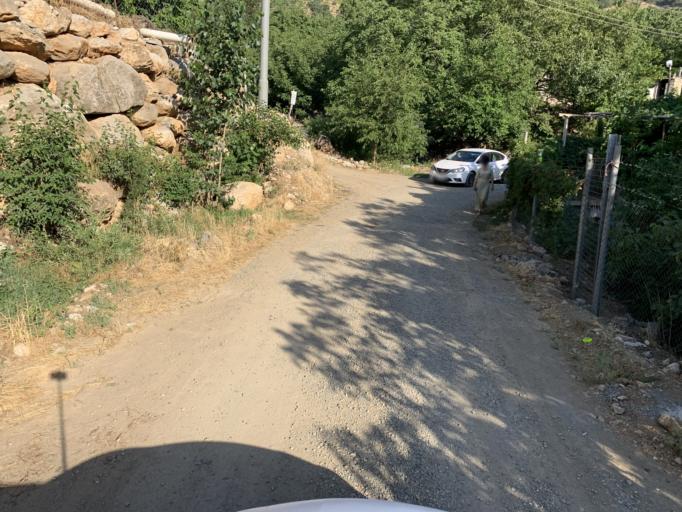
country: IQ
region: As Sulaymaniyah
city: Qeladize
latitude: 35.9892
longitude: 45.2003
